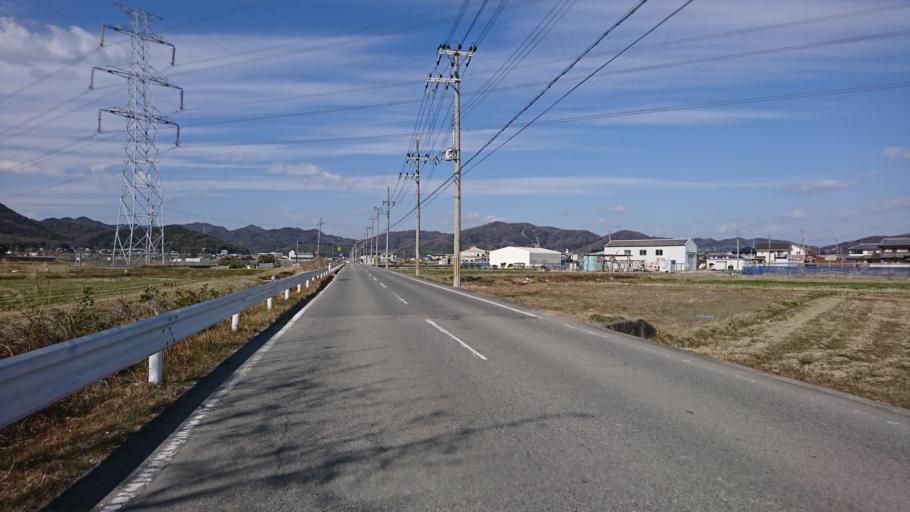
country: JP
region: Hyogo
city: Kakogawacho-honmachi
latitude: 34.8047
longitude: 134.8112
